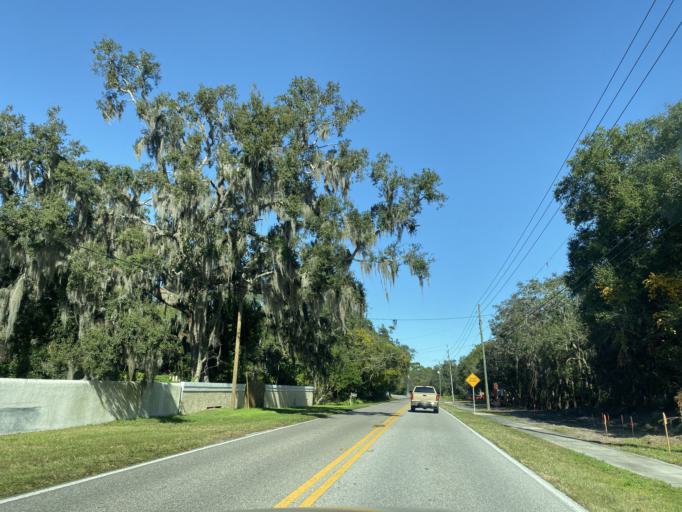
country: US
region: Florida
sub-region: Seminole County
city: Goldenrod
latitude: 28.6050
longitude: -81.2429
